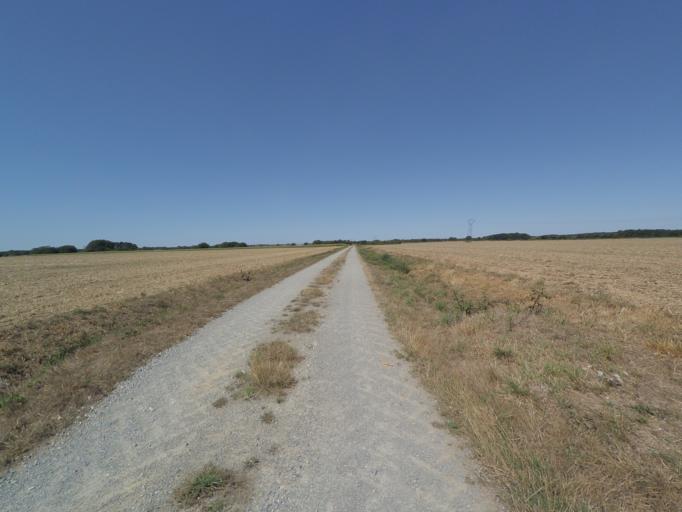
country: FR
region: Pays de la Loire
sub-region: Departement de la Loire-Atlantique
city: La Planche
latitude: 46.9946
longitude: -1.4133
